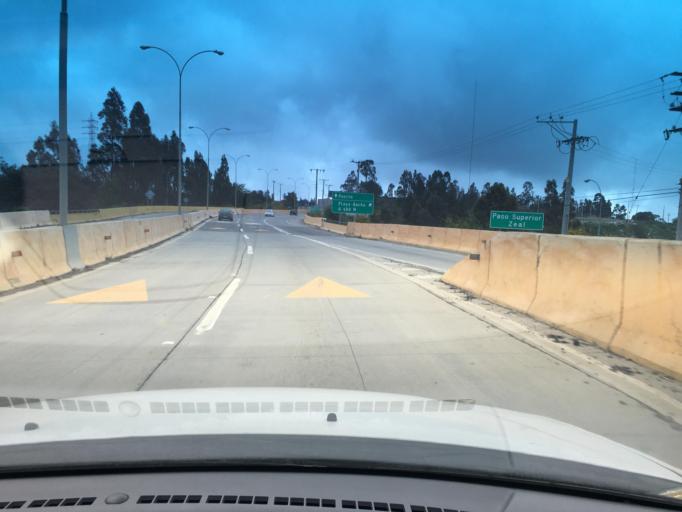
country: CL
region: Valparaiso
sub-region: Provincia de Valparaiso
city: Valparaiso
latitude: -33.0718
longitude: -71.6276
